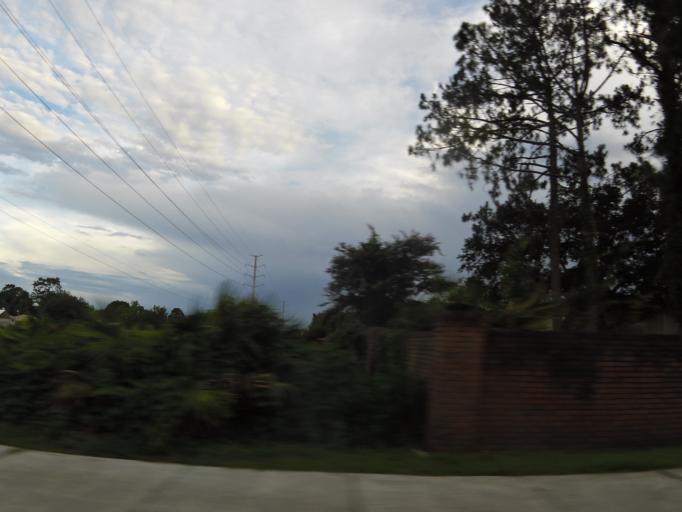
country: US
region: Florida
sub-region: Clay County
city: Bellair-Meadowbrook Terrace
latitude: 30.3020
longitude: -81.8206
